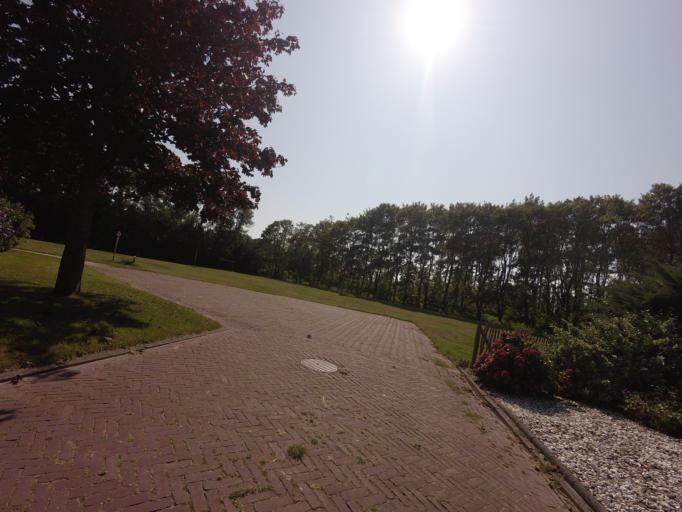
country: NL
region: Groningen
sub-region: Gemeente De Marne
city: Ulrum
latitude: 53.3594
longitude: 6.2903
